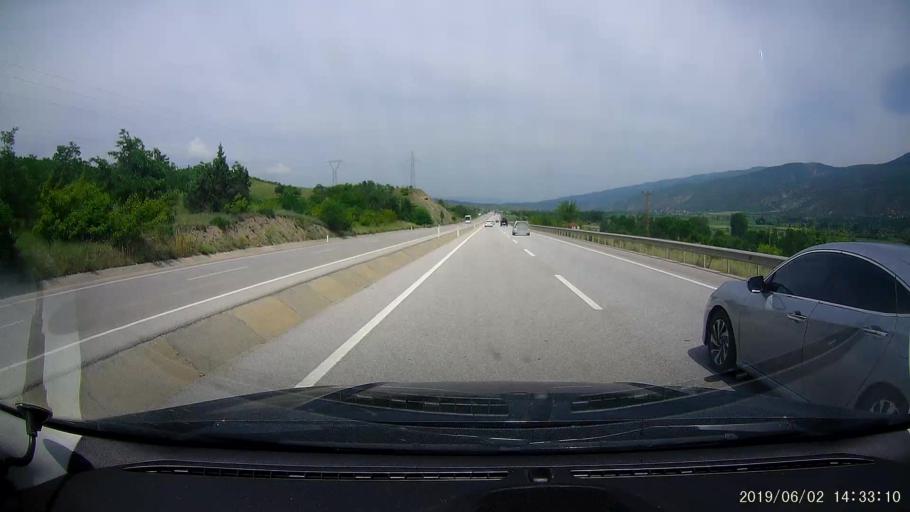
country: TR
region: Kastamonu
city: Tosya
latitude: 41.0296
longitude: 34.1642
